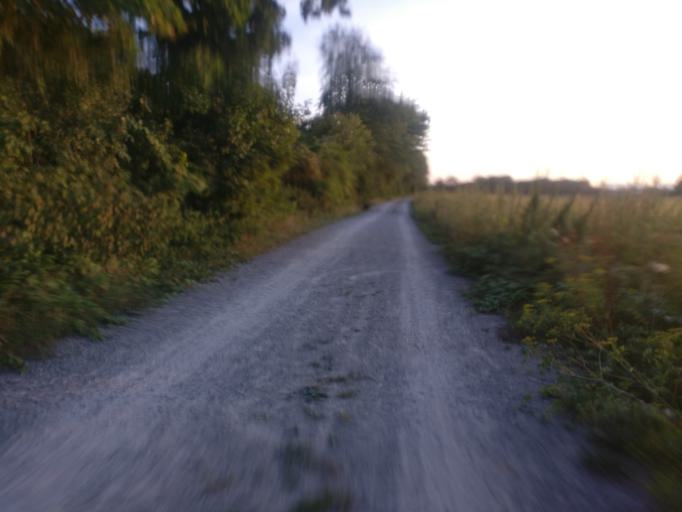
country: AT
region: Lower Austria
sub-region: Politischer Bezirk Baden
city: Ebreichsdorf
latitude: 47.9592
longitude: 16.4243
